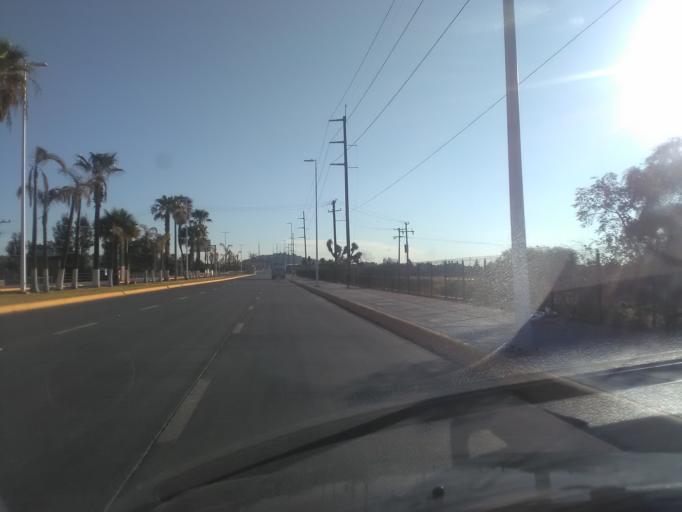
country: MX
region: Durango
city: Victoria de Durango
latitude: 24.0008
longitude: -104.6993
